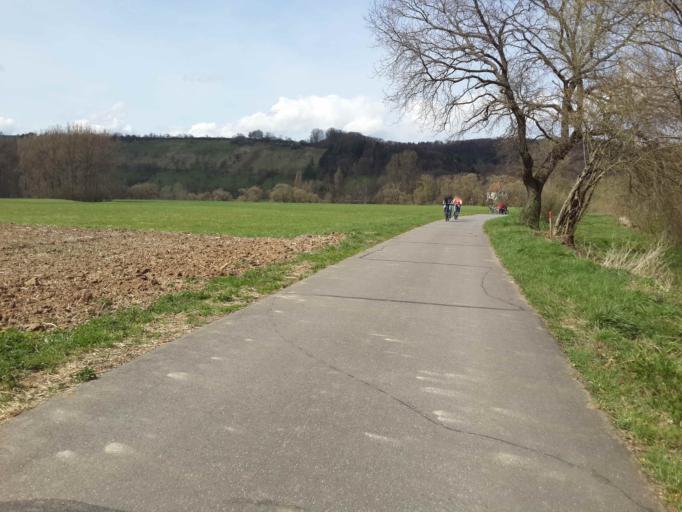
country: DE
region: Baden-Wuerttemberg
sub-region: Regierungsbezirk Stuttgart
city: Krautheim
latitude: 49.3901
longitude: 9.6573
